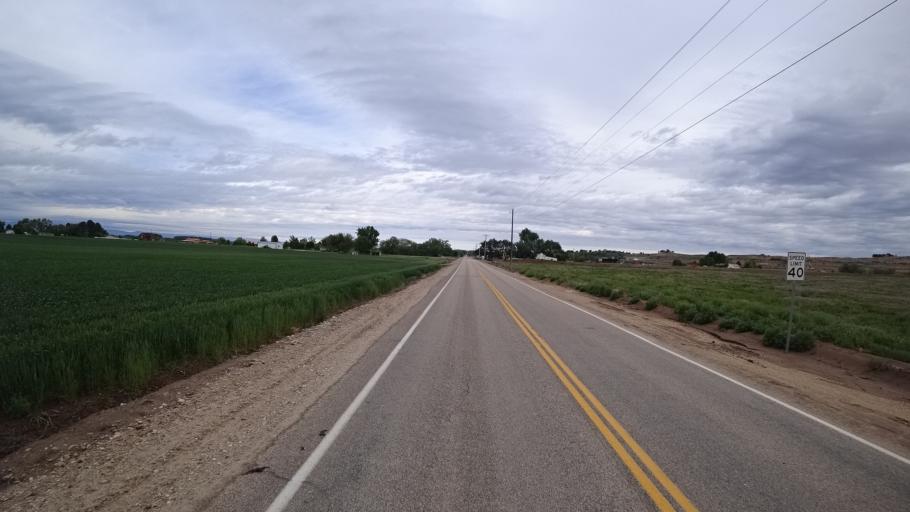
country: US
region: Idaho
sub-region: Ada County
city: Star
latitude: 43.7174
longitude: -116.4845
